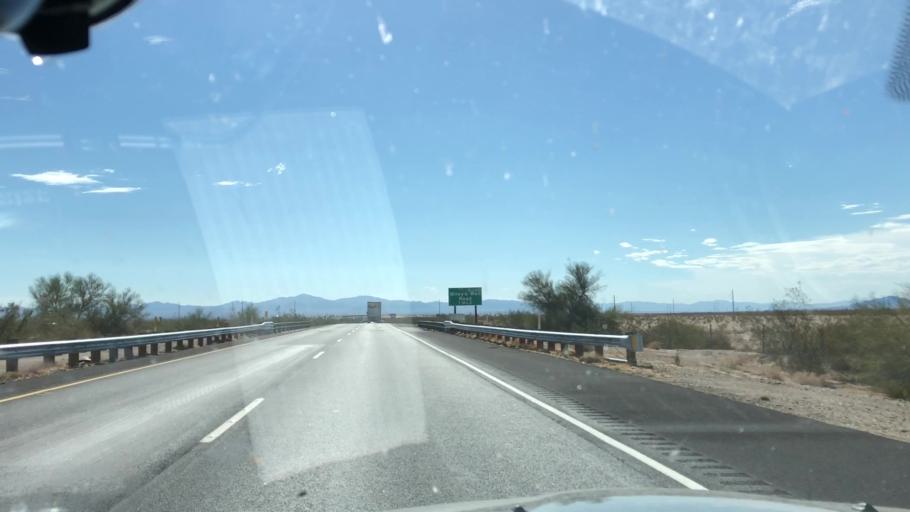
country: US
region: California
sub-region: Riverside County
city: Mesa Verde
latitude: 33.6087
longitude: -114.8817
